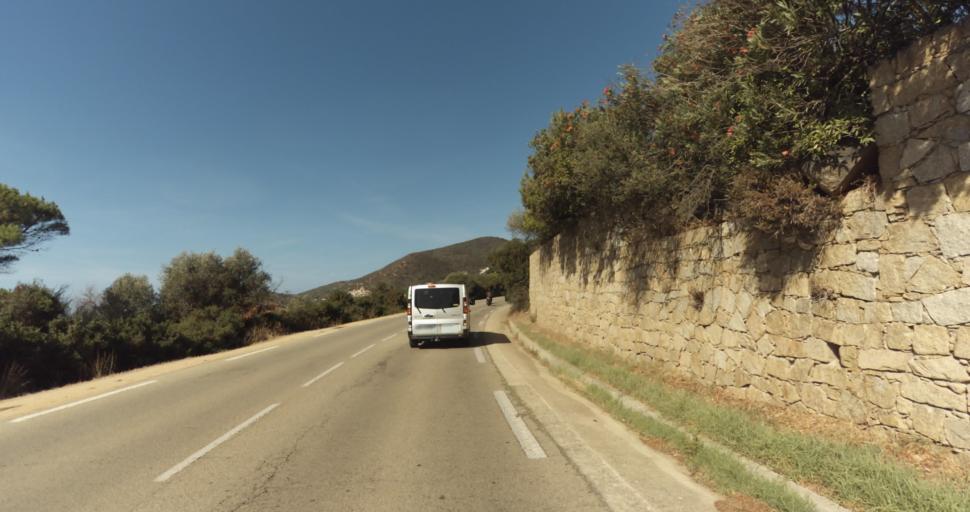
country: FR
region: Corsica
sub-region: Departement de la Corse-du-Sud
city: Ajaccio
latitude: 41.9094
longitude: 8.6503
